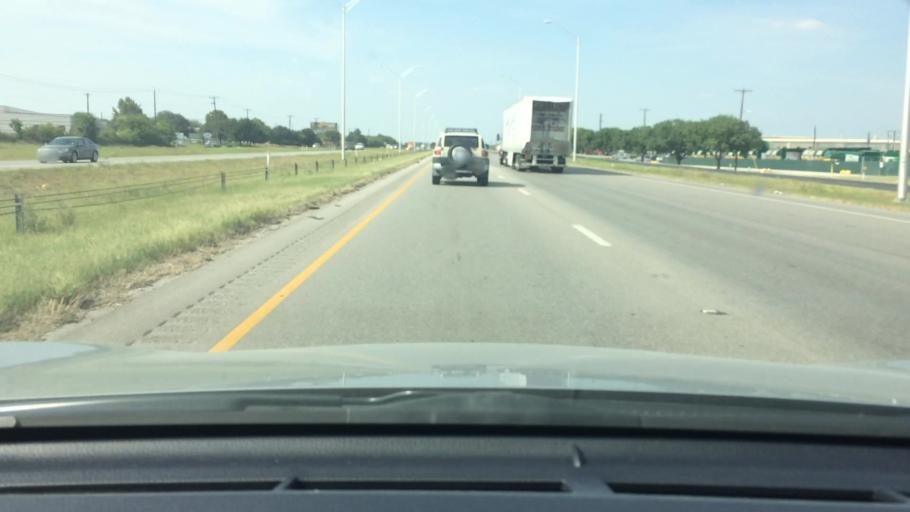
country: US
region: Texas
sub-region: Bexar County
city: China Grove
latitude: 29.3762
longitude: -98.3935
